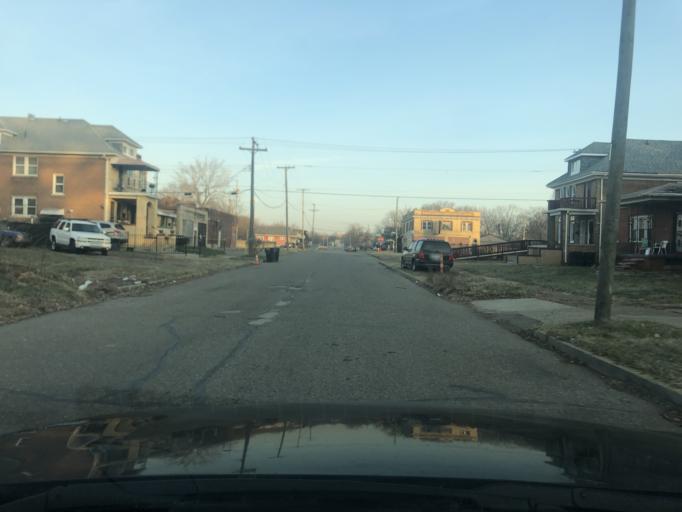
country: US
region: Michigan
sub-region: Wayne County
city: Highland Park
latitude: 42.4019
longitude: -83.1379
